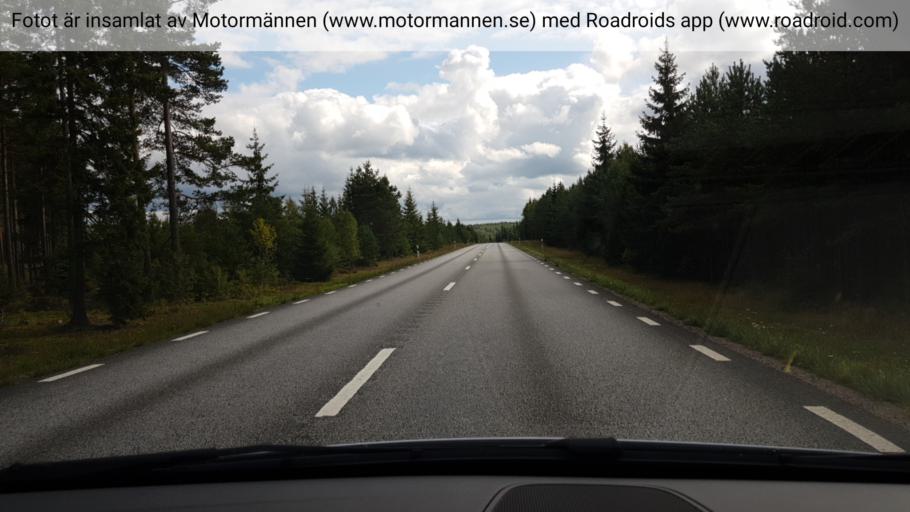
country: SE
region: Joenkoeping
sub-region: Mullsjo Kommun
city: Mullsjoe
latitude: 58.0431
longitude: 13.8239
